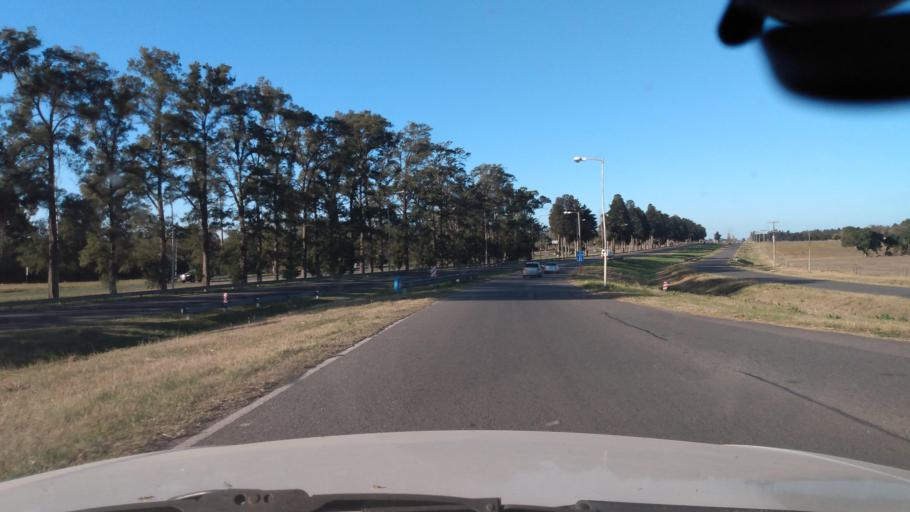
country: AR
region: Buenos Aires
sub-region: Partido de Lujan
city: Lujan
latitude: -34.6330
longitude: -59.2478
